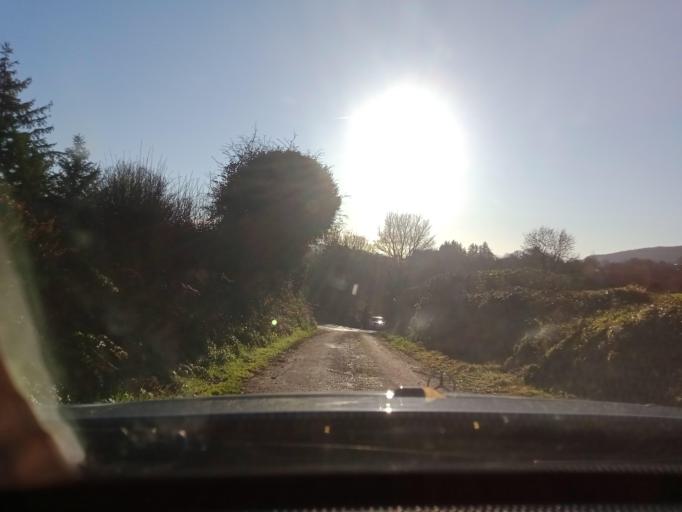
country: IE
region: Munster
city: Carrick-on-Suir
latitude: 52.4301
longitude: -7.3937
